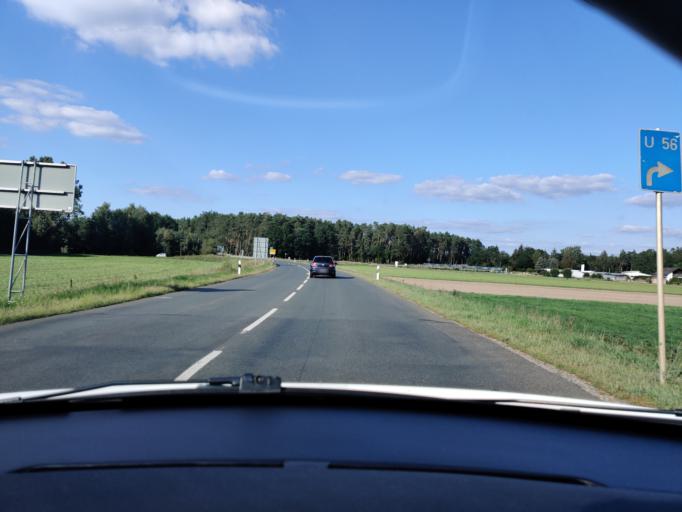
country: DE
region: Bavaria
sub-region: Upper Palatinate
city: Schwarzenfeld
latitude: 49.3480
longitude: 12.1447
